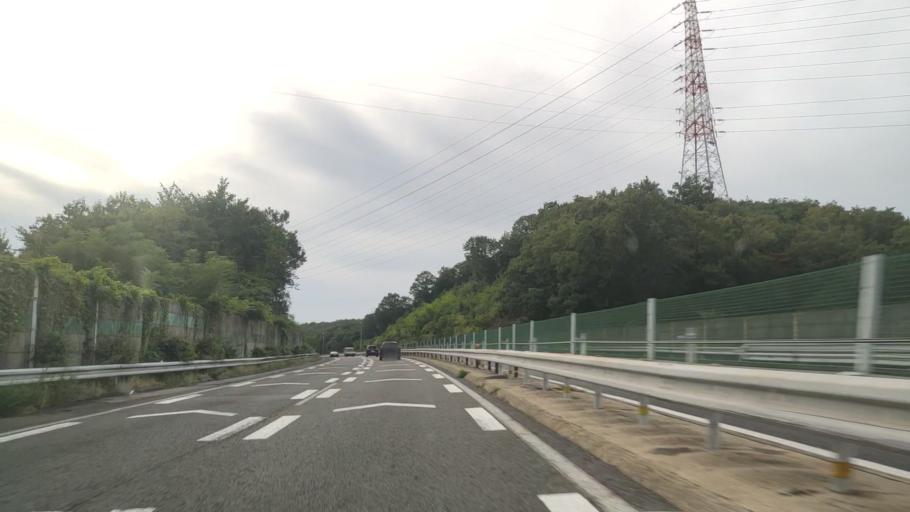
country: JP
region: Gifu
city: Tajimi
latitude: 35.3520
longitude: 137.1326
